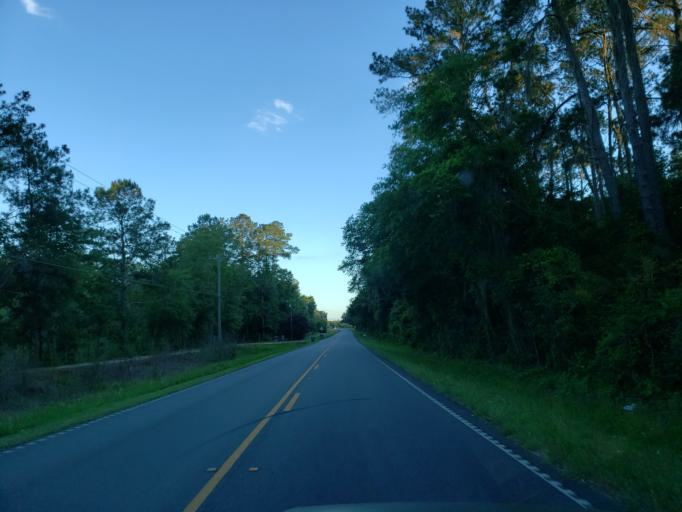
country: US
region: Georgia
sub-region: Lowndes County
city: Valdosta
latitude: 30.7311
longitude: -83.2488
